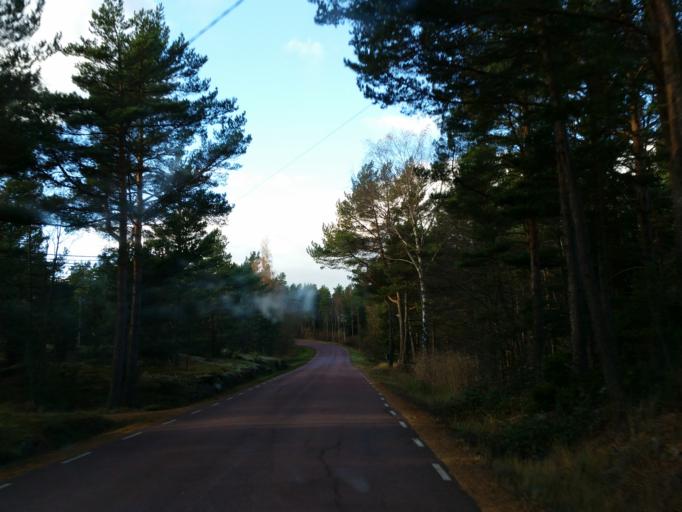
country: AX
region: Alands skaergard
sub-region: Foegloe
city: Foegloe
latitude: 60.0469
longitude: 20.5199
